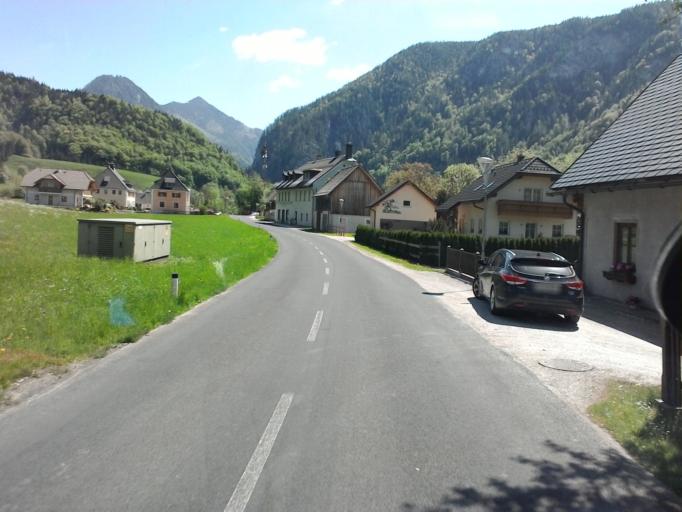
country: AT
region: Styria
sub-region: Politischer Bezirk Liezen
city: Palfau
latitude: 47.7105
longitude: 14.8085
